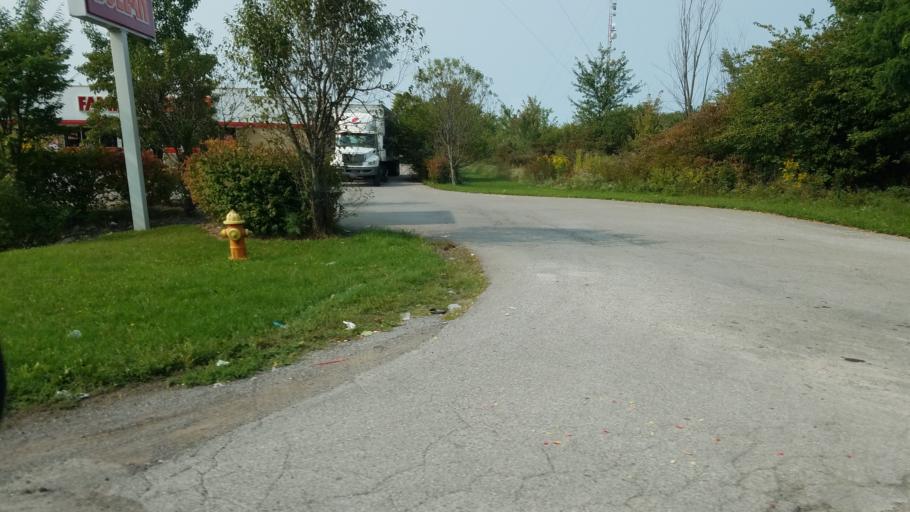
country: US
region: Ohio
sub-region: Mahoning County
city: Struthers
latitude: 41.0584
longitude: -80.6429
